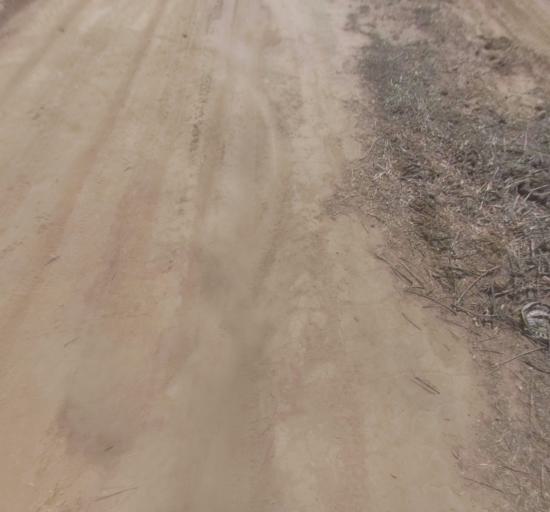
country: US
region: California
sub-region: Fresno County
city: Firebaugh
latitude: 37.0254
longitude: -120.4092
